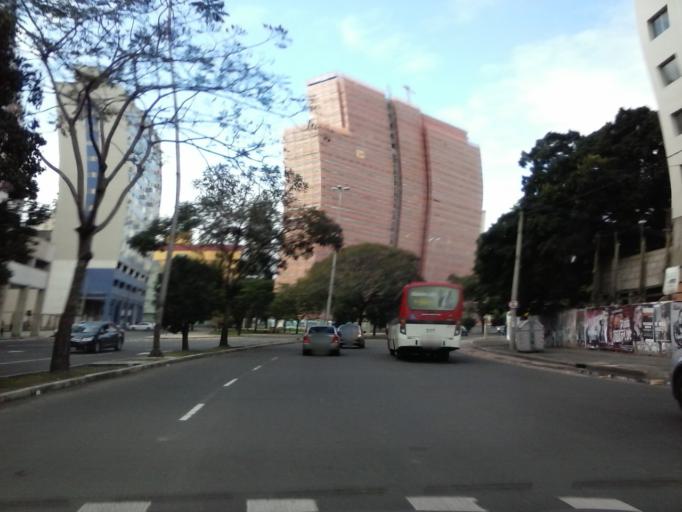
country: BR
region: Rio Grande do Sul
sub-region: Porto Alegre
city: Porto Alegre
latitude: -30.0358
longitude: -51.2246
